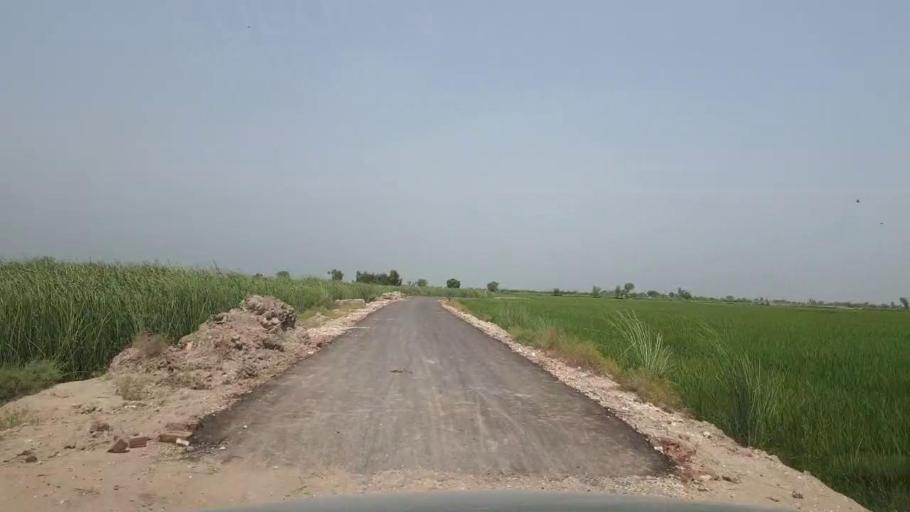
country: PK
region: Sindh
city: Garhi Yasin
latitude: 27.9279
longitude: 68.4330
